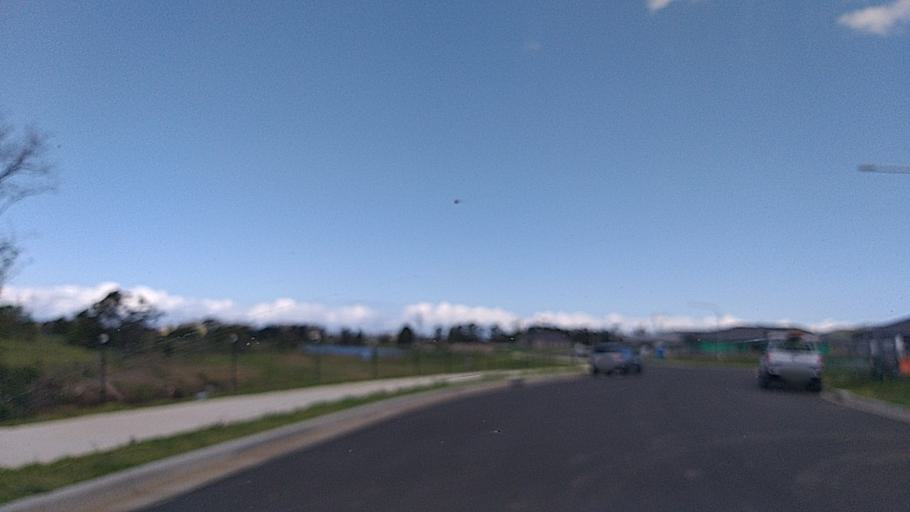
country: AU
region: New South Wales
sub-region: Wollongong
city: Dapto
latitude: -34.4755
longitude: 150.7652
